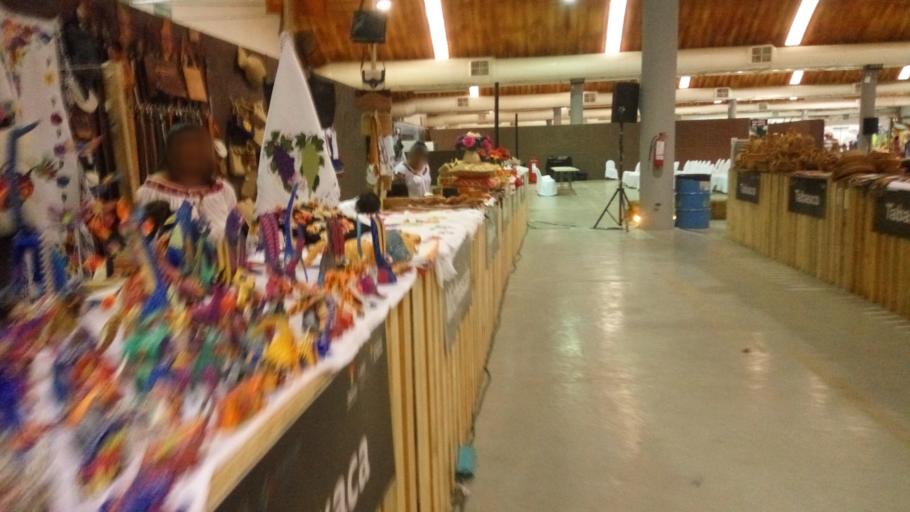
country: MX
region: Tabasco
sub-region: Nacajuca
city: Bosque de Saloya
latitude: 18.0071
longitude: -92.9629
